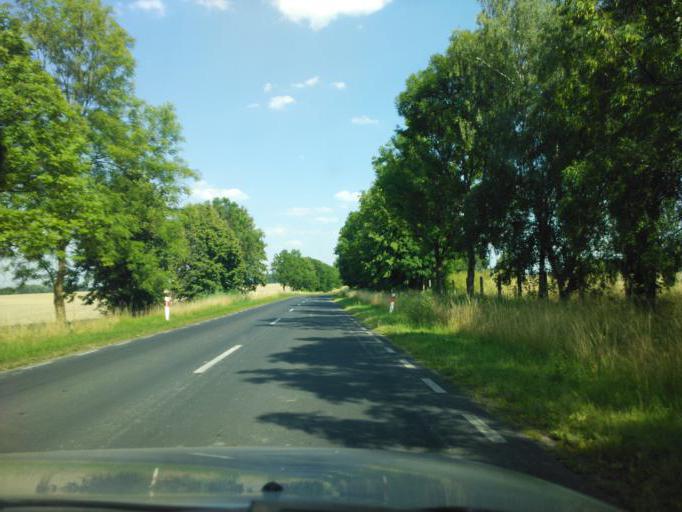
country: PL
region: West Pomeranian Voivodeship
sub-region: Powiat pyrzycki
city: Pyrzyce
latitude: 53.1367
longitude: 14.9275
